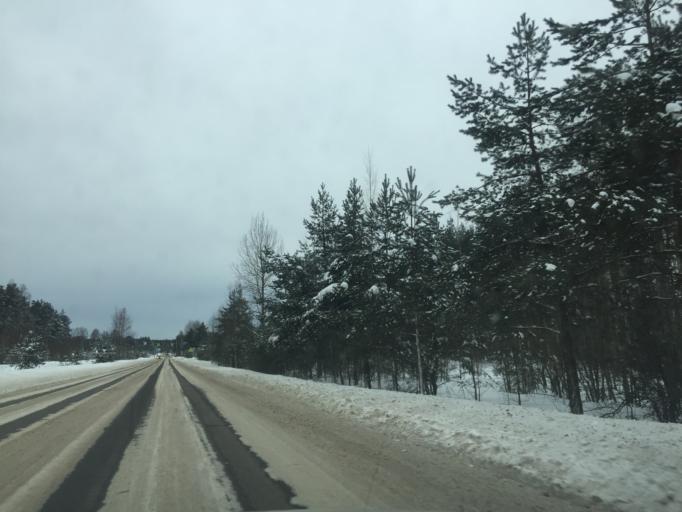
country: RU
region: Leningrad
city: Koltushi
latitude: 59.8678
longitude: 30.6709
